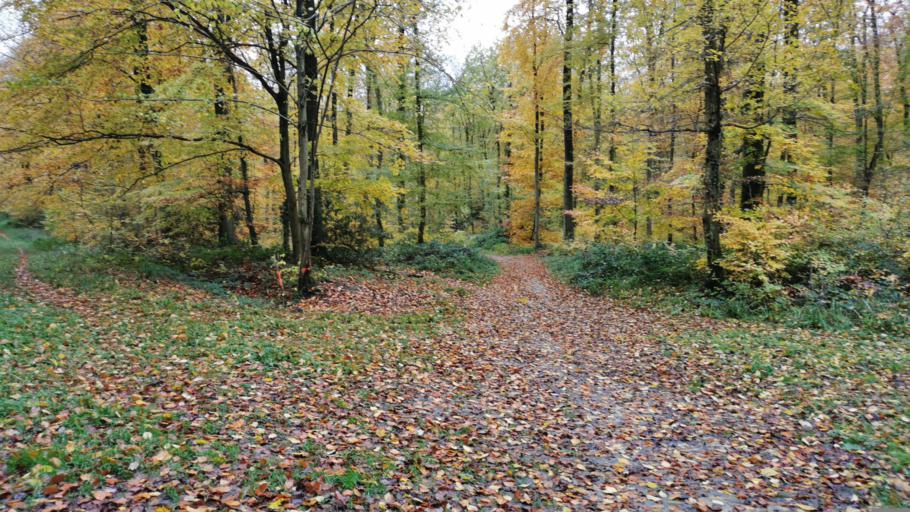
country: FR
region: Picardie
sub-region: Departement de l'Aisne
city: Saint-Gobain
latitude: 49.5902
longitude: 3.3723
